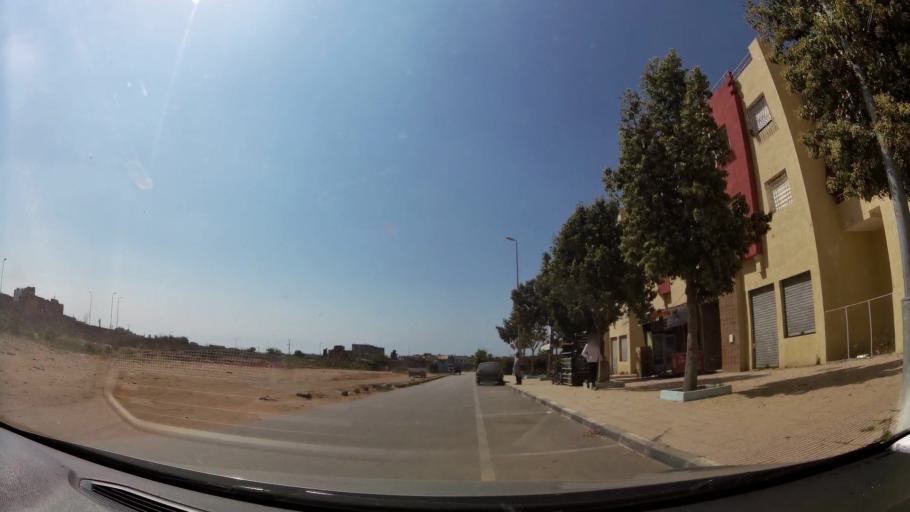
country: MA
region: Rabat-Sale-Zemmour-Zaer
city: Sale
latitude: 34.0702
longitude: -6.7566
